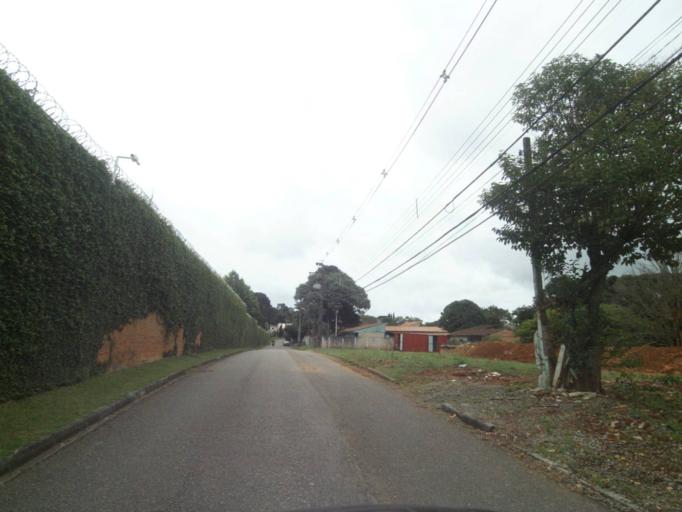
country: BR
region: Parana
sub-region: Curitiba
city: Curitiba
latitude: -25.4526
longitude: -49.3329
